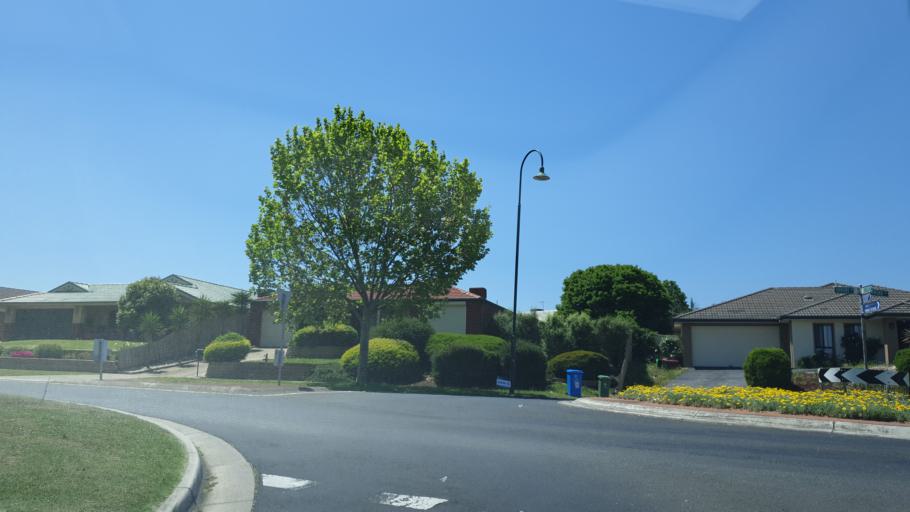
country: AU
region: Victoria
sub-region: Casey
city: Narre Warren South
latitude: -38.0627
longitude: 145.2925
